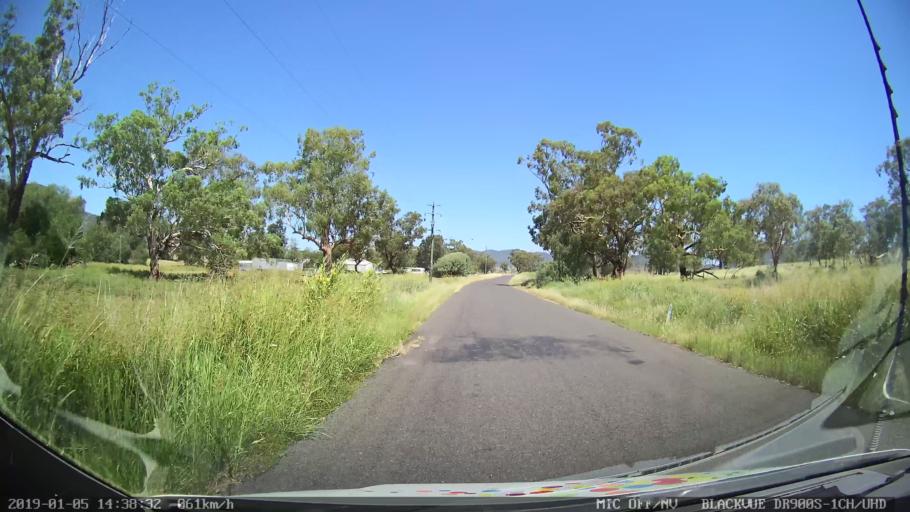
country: AU
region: New South Wales
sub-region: Tamworth Municipality
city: Phillip
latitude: -31.2496
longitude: 150.6923
